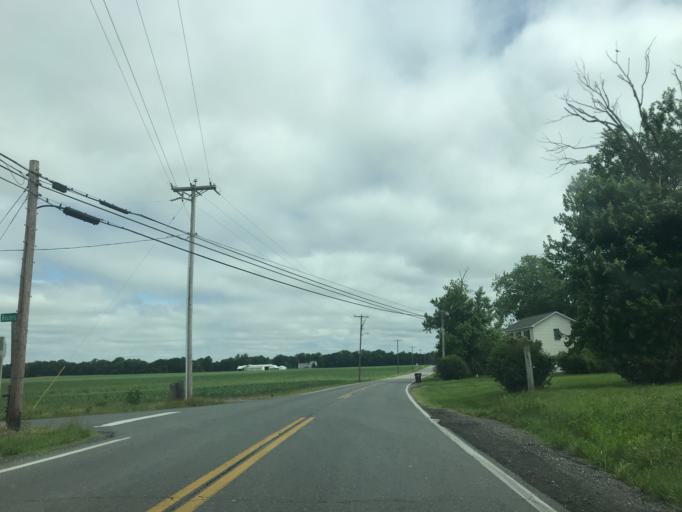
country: US
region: Maryland
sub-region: Caroline County
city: Ridgely
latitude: 38.9061
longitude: -75.9584
